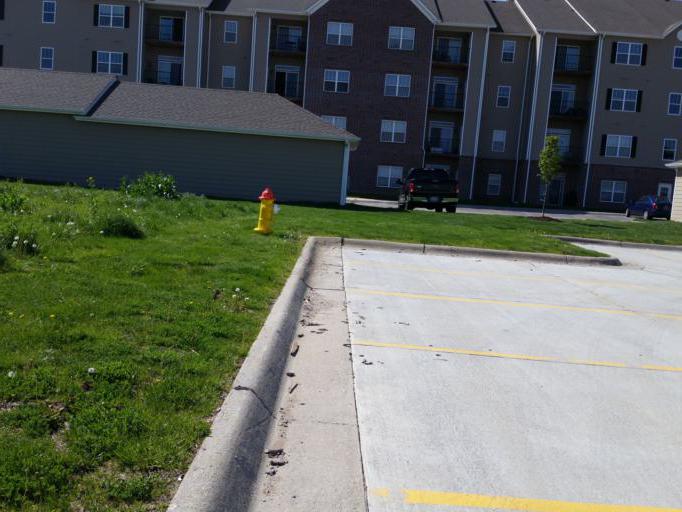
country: US
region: Nebraska
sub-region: Sarpy County
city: Offutt Air Force Base
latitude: 41.1461
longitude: -95.9725
